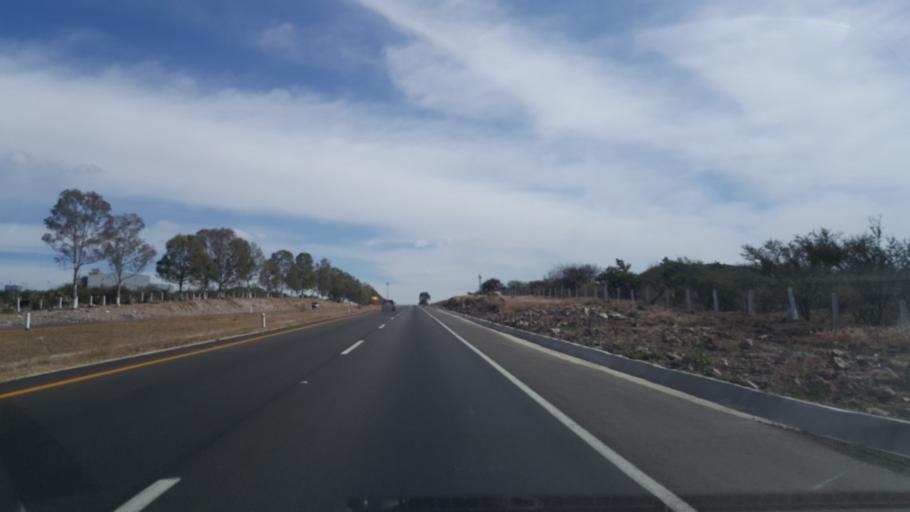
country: MX
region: Jalisco
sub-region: Lagos de Moreno
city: Cristeros [Fraccionamiento]
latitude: 21.2677
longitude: -101.9681
